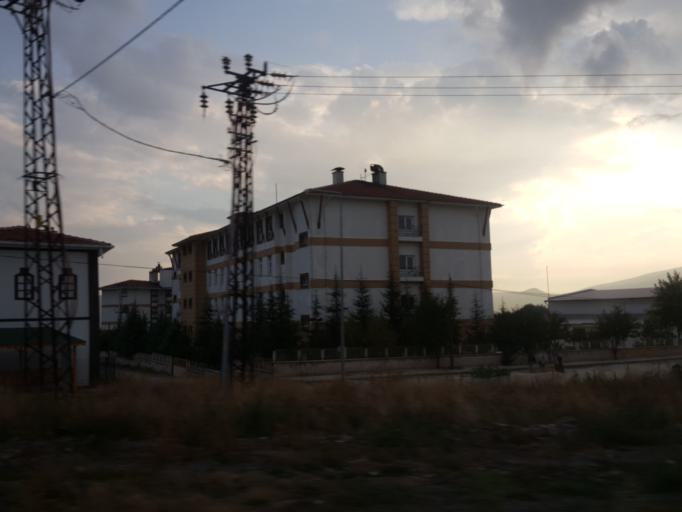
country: TR
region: Amasya
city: Gumushacikoy
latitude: 40.8780
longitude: 35.2293
